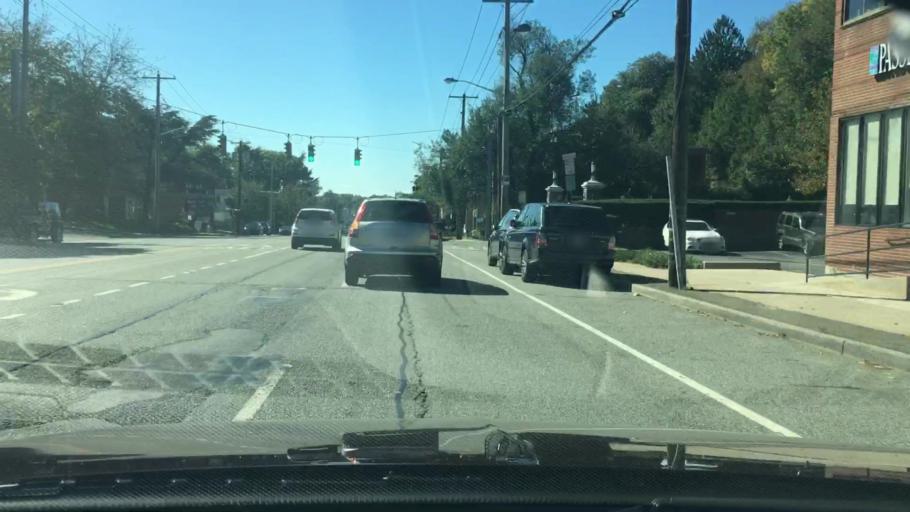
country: US
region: New York
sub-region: Nassau County
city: University Gardens
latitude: 40.7790
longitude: -73.7236
